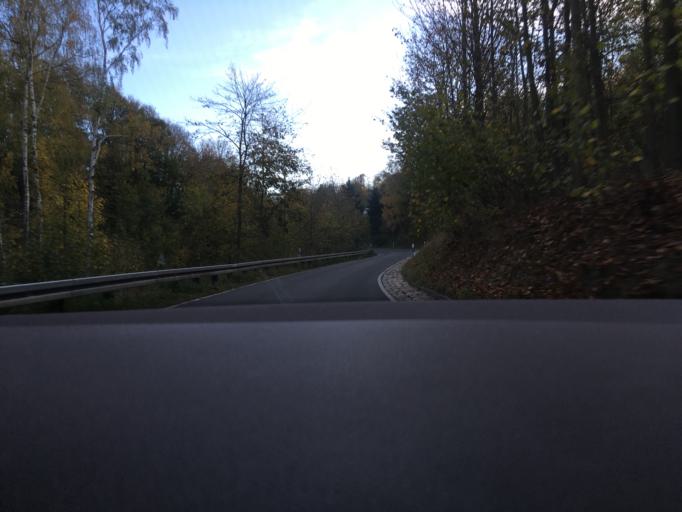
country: DE
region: Saxony
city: Glashutte
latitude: 50.8433
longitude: 13.7991
